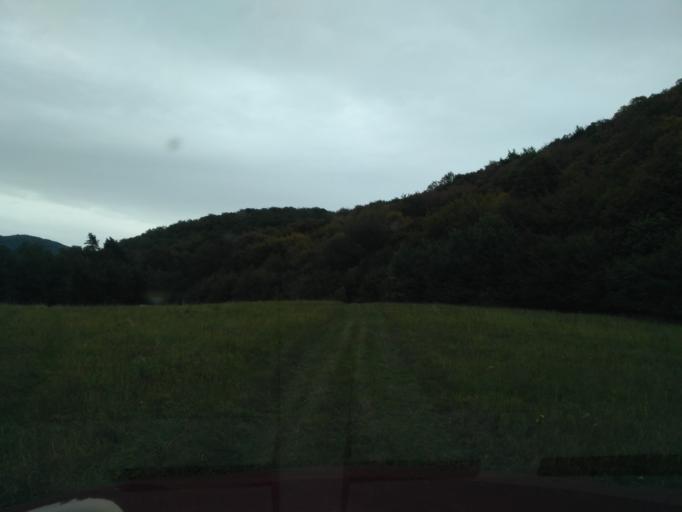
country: SK
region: Presovsky
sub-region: Okres Presov
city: Presov
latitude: 48.8948
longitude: 21.3410
